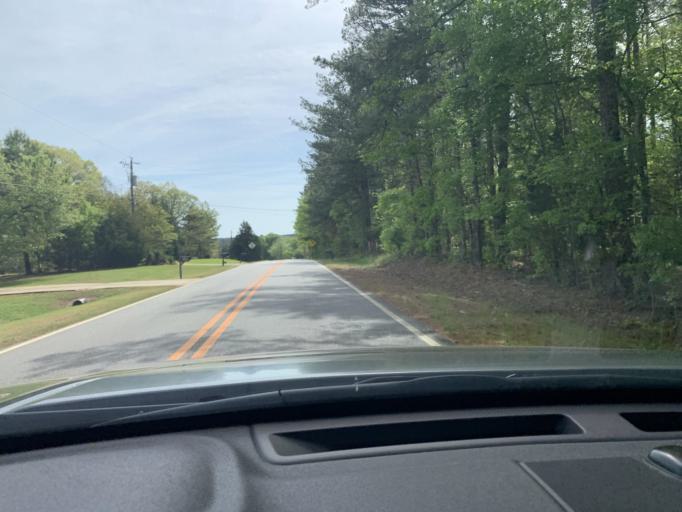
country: US
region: Georgia
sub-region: Oconee County
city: Watkinsville
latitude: 33.8406
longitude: -83.4832
